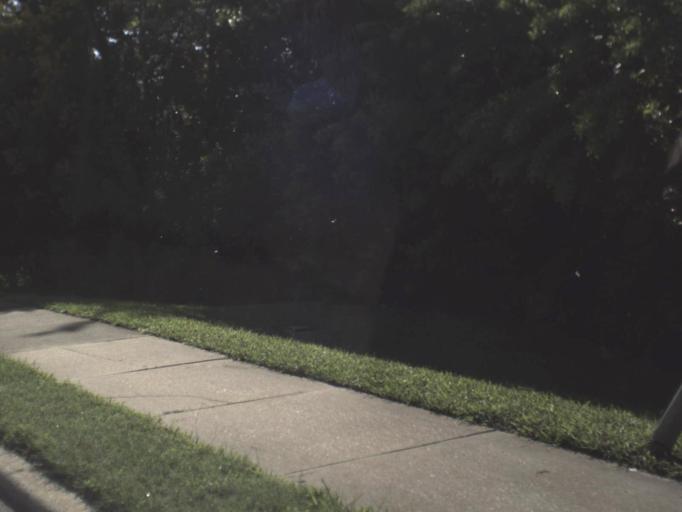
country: US
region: Florida
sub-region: Sarasota County
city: Sarasota
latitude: 27.3284
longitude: -82.5364
